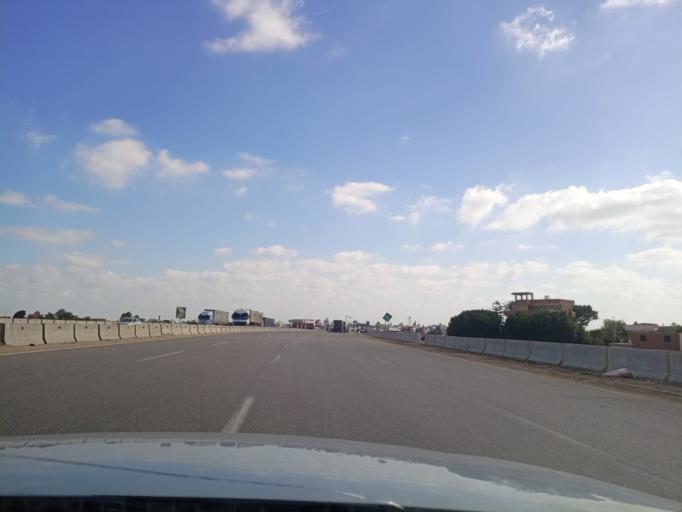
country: EG
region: Muhafazat al Minufiyah
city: Ashmun
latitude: 30.3339
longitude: 30.8413
